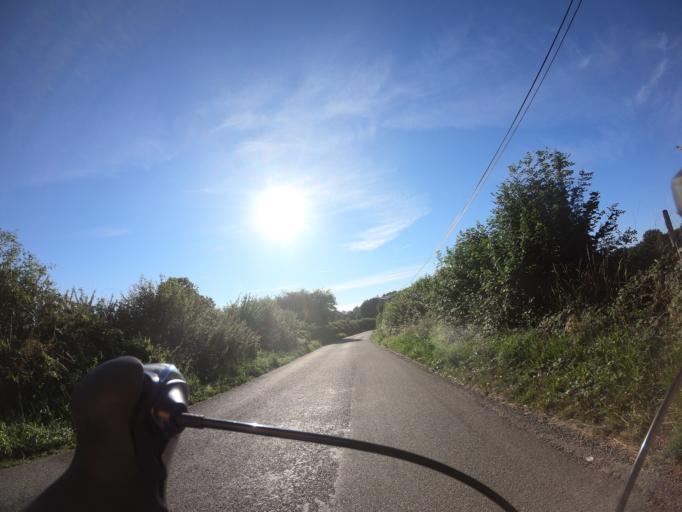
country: FR
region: Pays de la Loire
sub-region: Departement de la Mayenne
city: Pre-en-Pail
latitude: 48.5433
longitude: -0.2250
